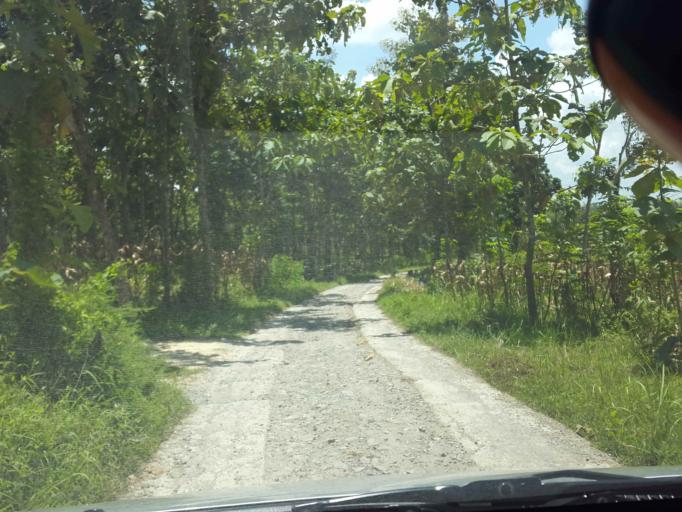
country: ID
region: Central Java
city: Sragen
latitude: -7.2722
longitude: 111.1302
